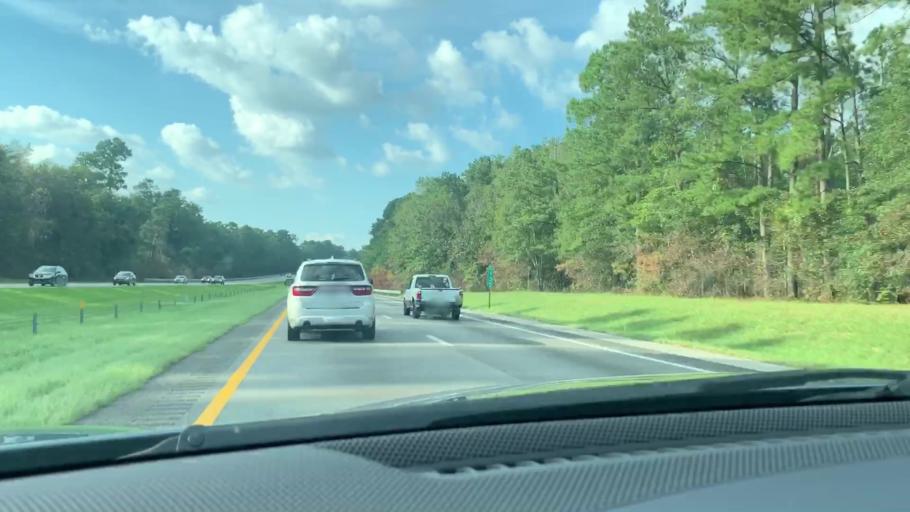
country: US
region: South Carolina
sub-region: Calhoun County
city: Oak Grove
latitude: 33.6895
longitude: -80.9094
